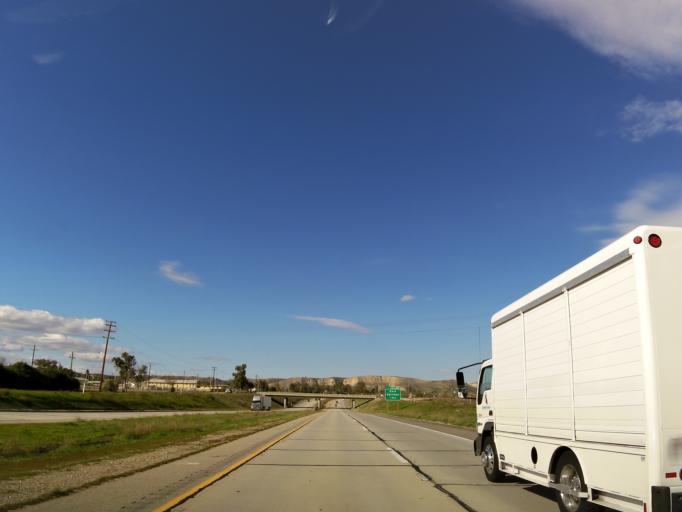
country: US
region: California
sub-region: San Luis Obispo County
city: San Miguel
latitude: 35.7977
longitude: -120.7402
